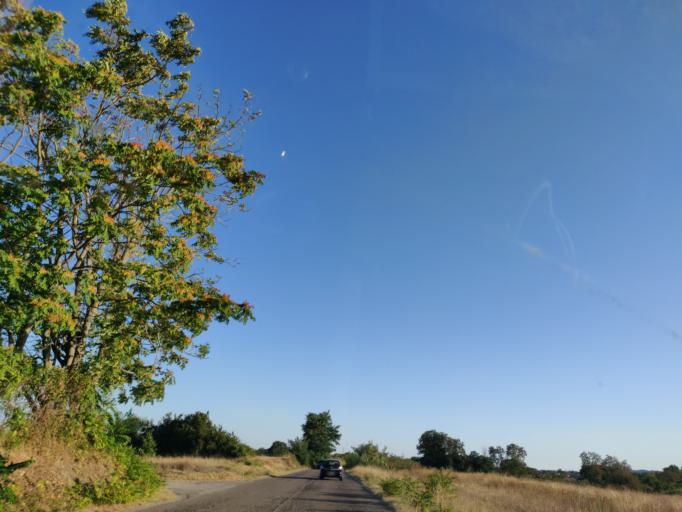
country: IT
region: Latium
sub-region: Provincia di Viterbo
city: Grotte di Castro
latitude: 42.6933
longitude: 11.8779
